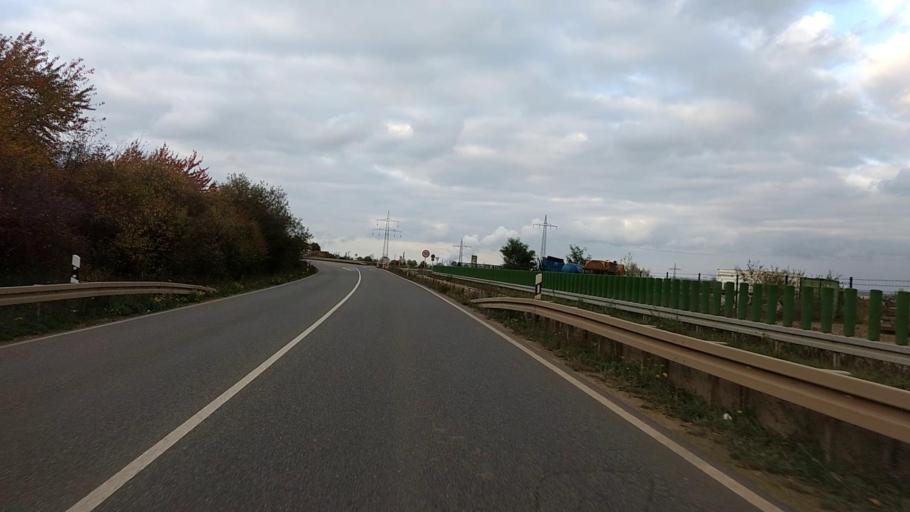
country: DE
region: North Rhine-Westphalia
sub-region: Regierungsbezirk Koln
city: Kerpen
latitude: 50.8837
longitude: 6.6436
